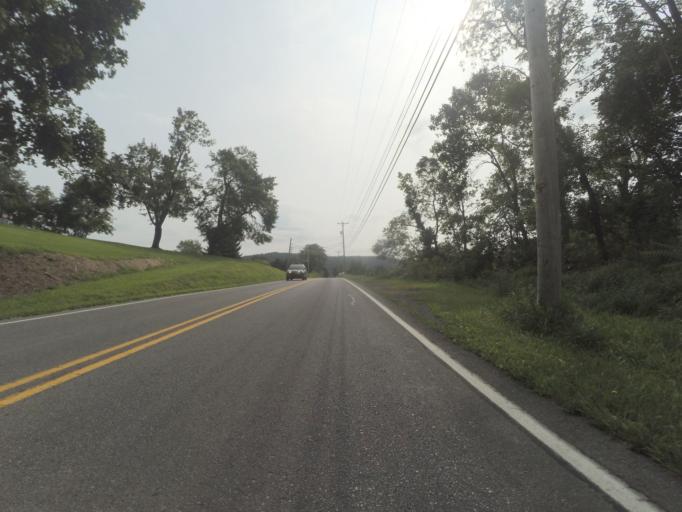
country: US
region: Pennsylvania
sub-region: Huntingdon County
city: Huntingdon
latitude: 40.5679
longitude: -78.0611
